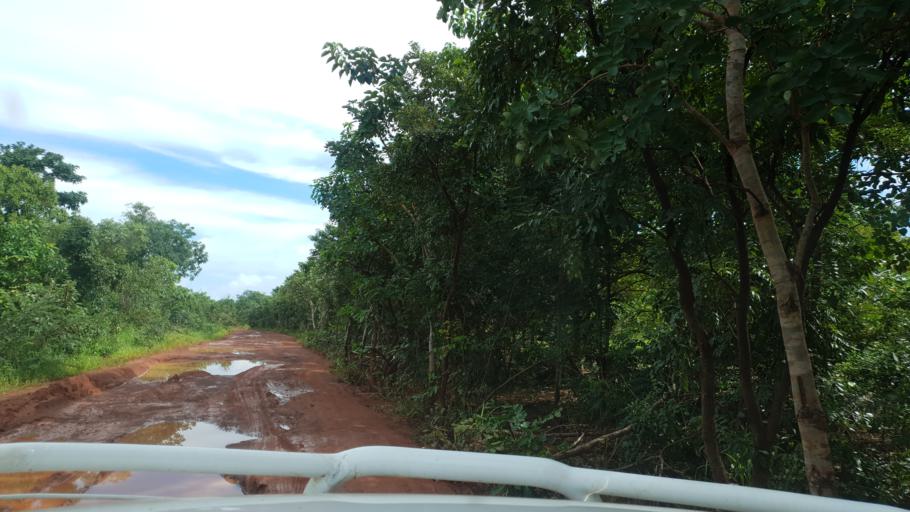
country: ML
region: Sikasso
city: Kolondieba
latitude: 10.7469
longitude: -6.9125
